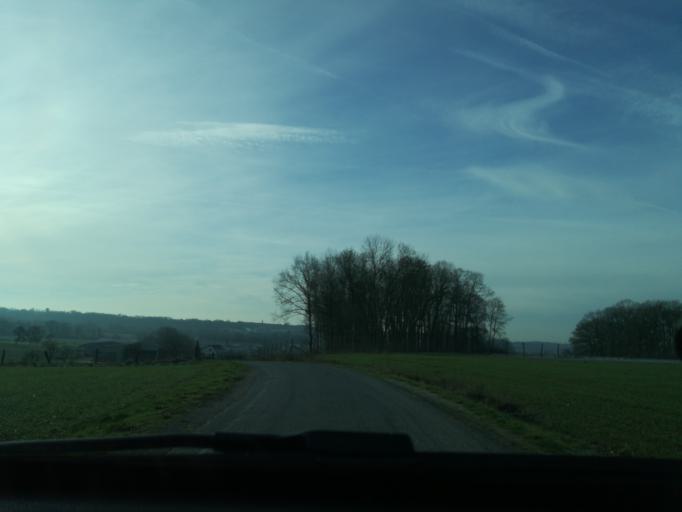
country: FR
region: Lorraine
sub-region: Departement de la Meuse
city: Revigny-sur-Ornain
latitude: 48.8277
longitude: 5.0585
